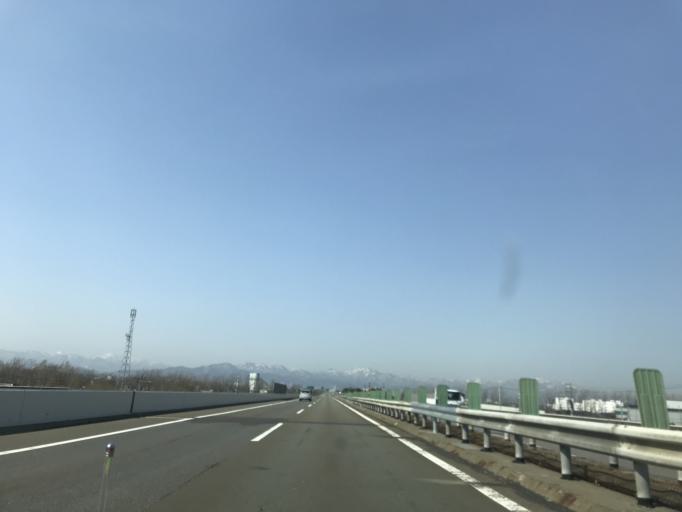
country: JP
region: Hokkaido
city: Ebetsu
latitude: 43.0895
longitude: 141.4554
